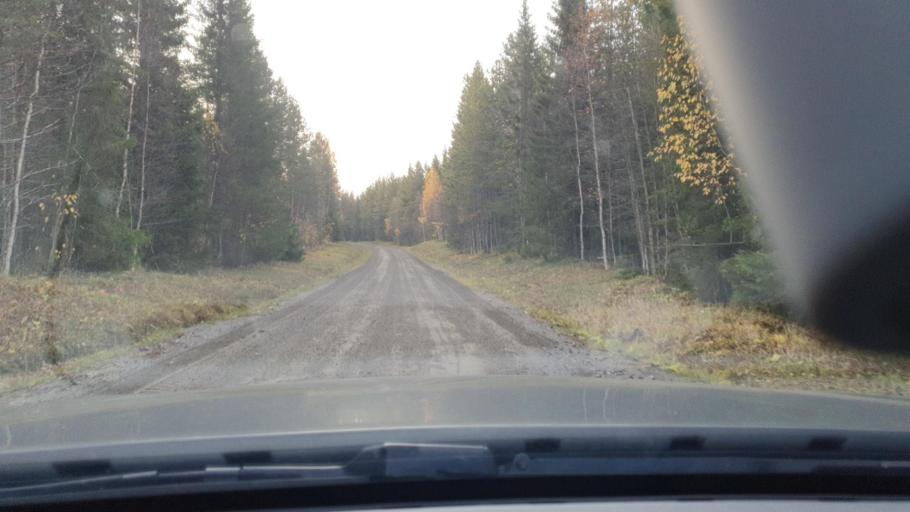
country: SE
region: Jaemtland
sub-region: Stroemsunds Kommun
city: Stroemsund
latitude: 63.5333
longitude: 15.6120
